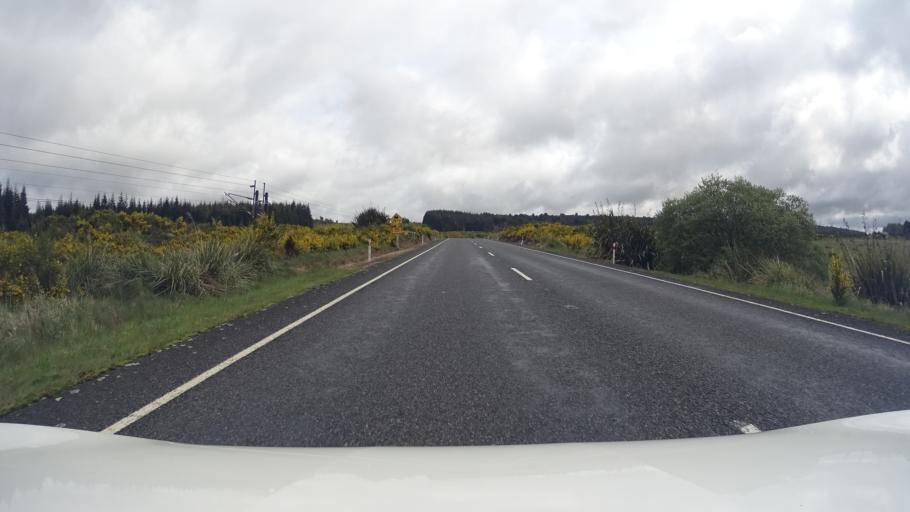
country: NZ
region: Manawatu-Wanganui
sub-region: Ruapehu District
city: Waiouru
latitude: -39.2083
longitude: 175.4023
